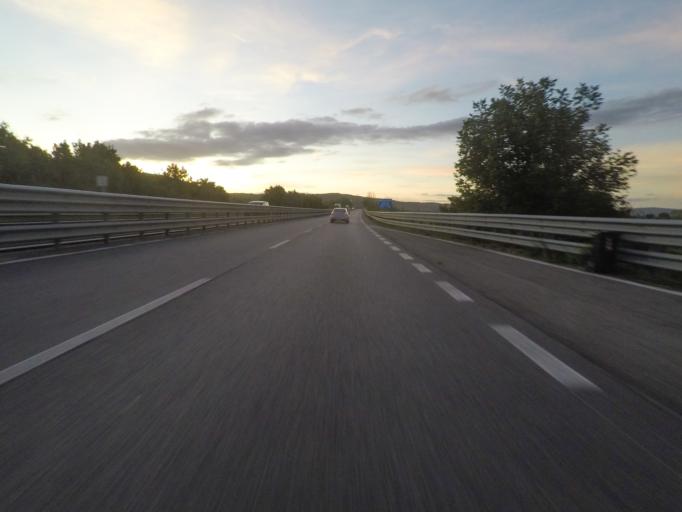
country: IT
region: Tuscany
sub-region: Provincia di Siena
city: Sinalunga
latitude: 43.2233
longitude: 11.7493
